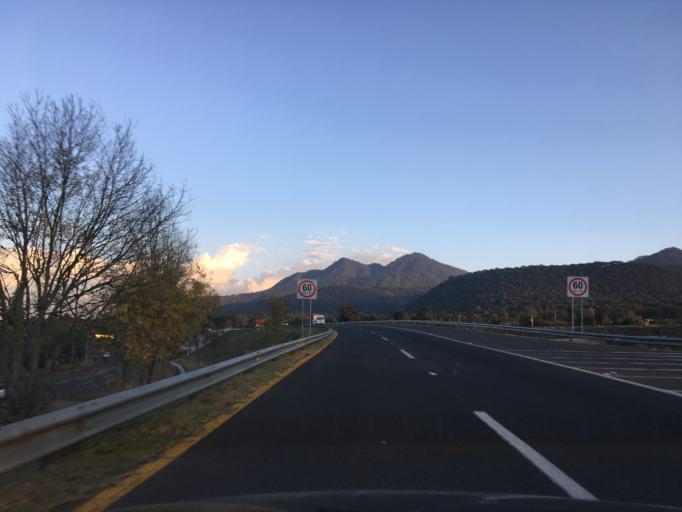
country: MX
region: Michoacan
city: Patzcuaro
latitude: 19.5312
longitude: -101.5638
